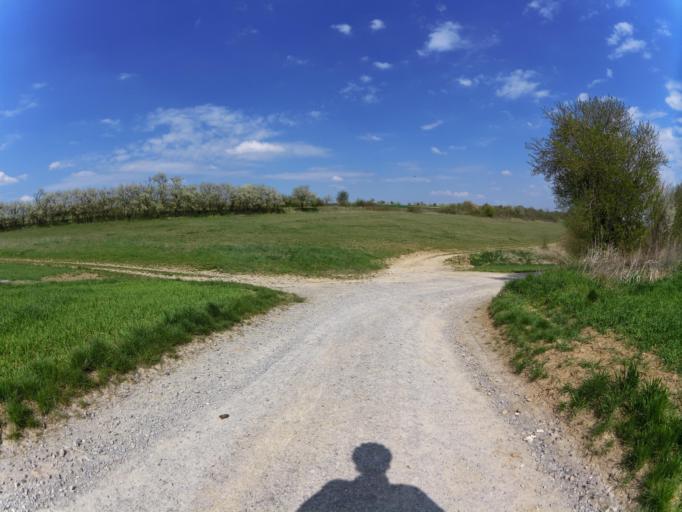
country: DE
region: Bavaria
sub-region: Regierungsbezirk Unterfranken
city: Winterhausen
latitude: 49.6867
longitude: 10.0097
